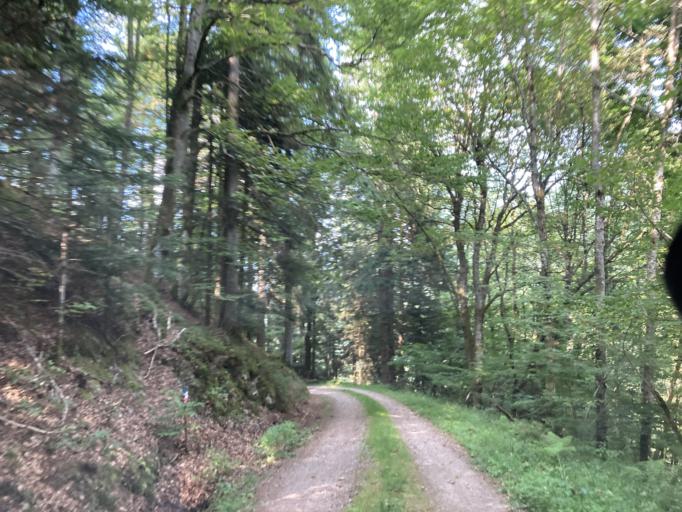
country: DE
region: Baden-Wuerttemberg
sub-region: Freiburg Region
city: Schonach im Schwarzwald
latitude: 48.1721
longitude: 8.1560
